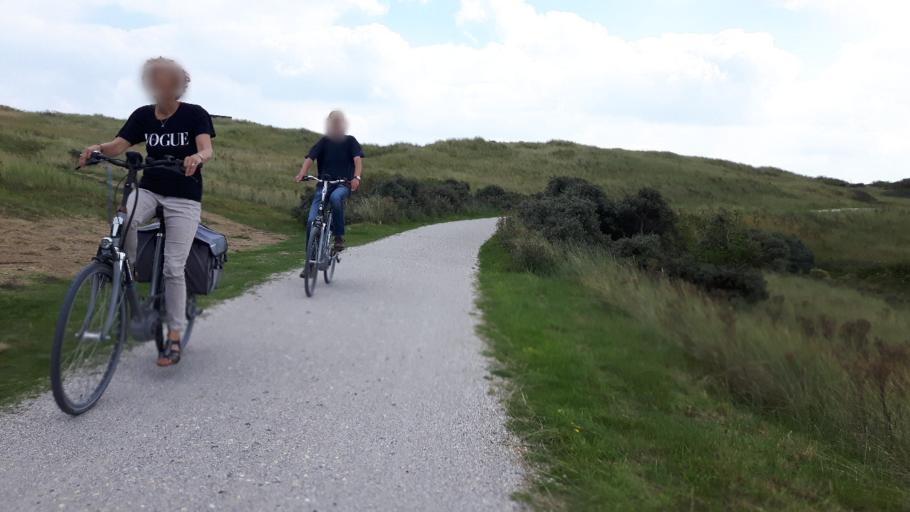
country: NL
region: Friesland
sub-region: Gemeente Dongeradeel
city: Holwerd
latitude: 53.4600
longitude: 5.9012
